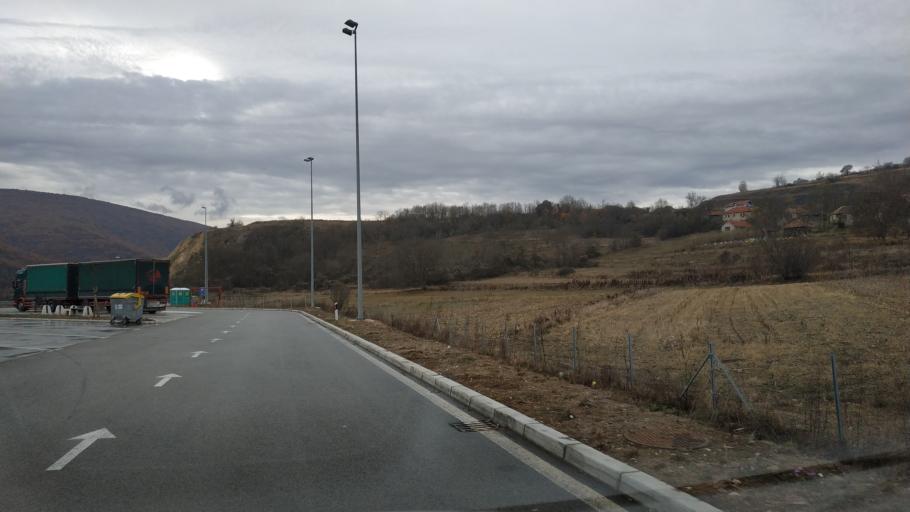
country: RS
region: Central Serbia
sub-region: Pirotski Okrug
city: Bela Palanka
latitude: 43.2296
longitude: 22.4339
